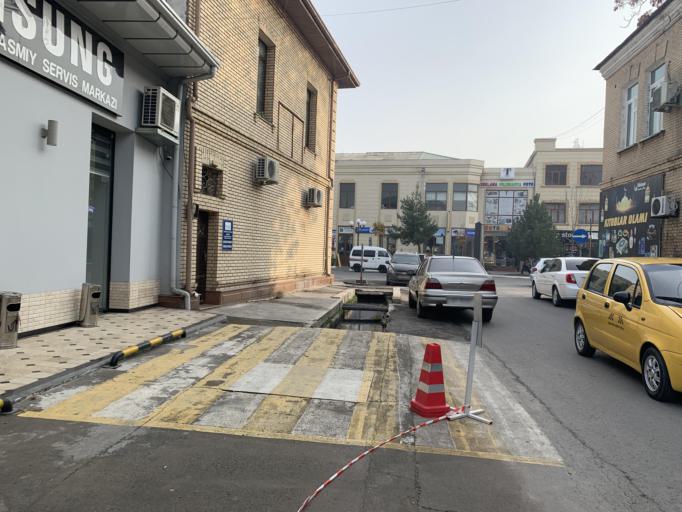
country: UZ
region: Fergana
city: Qo`qon
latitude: 40.5365
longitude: 70.9300
